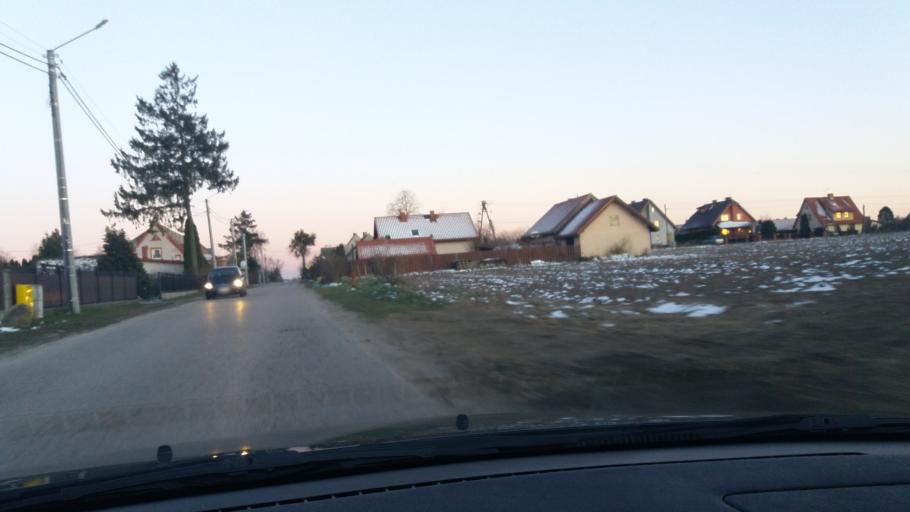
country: PL
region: Warmian-Masurian Voivodeship
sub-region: Powiat szczycienski
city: Szczytno
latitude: 53.5610
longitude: 20.9675
